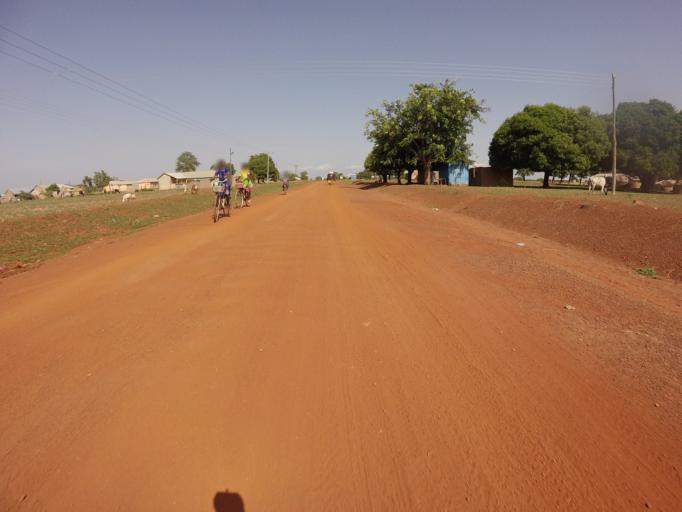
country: GH
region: Upper East
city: Bawku
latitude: 10.8340
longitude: -0.1738
